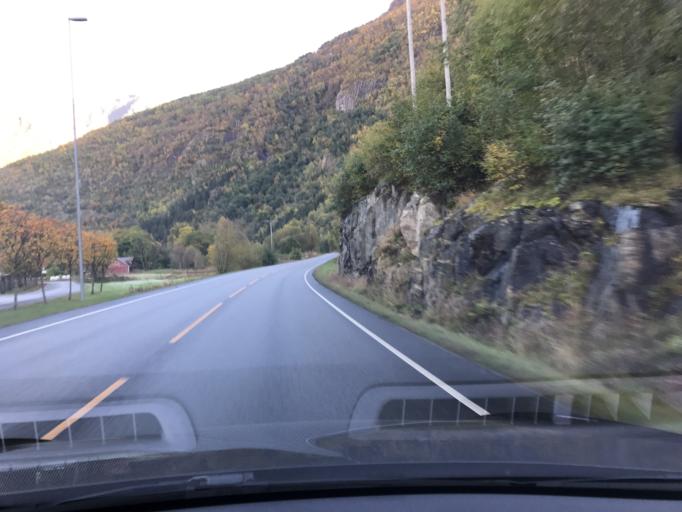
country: NO
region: Sogn og Fjordane
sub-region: Laerdal
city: Laerdalsoyri
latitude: 61.0973
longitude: 7.4753
